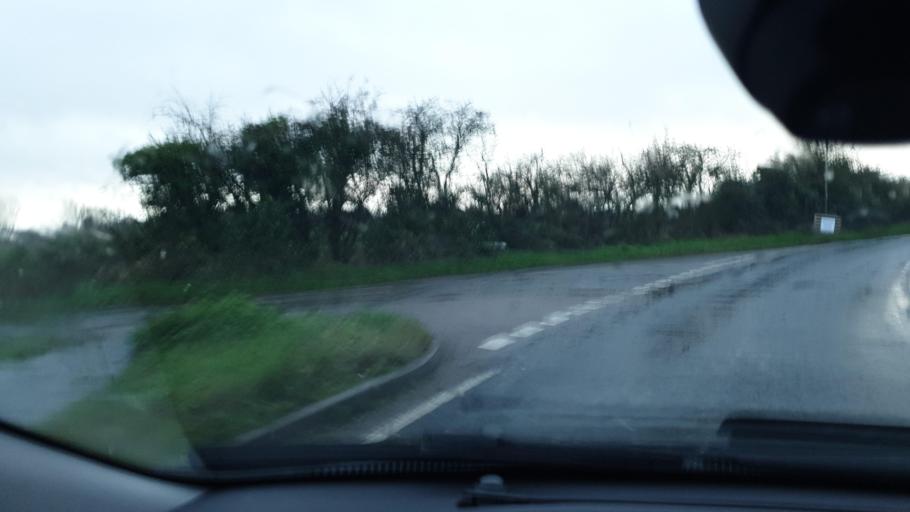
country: GB
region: England
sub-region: Suffolk
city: East Bergholt
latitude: 51.9261
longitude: 0.9918
